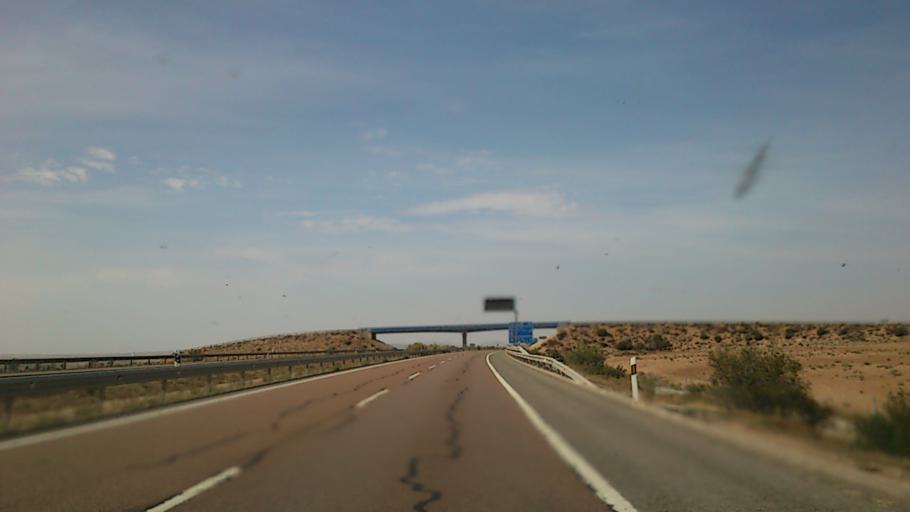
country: ES
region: Aragon
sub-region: Provincia de Teruel
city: Villafranca del Campo
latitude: 40.6886
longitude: -1.3189
